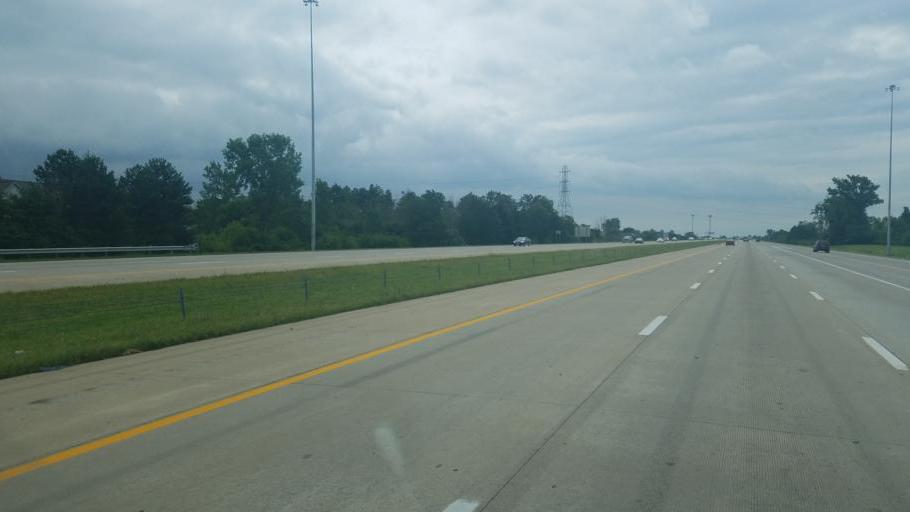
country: US
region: Ohio
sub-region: Franklin County
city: Lincoln Village
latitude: 39.9202
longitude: -83.1165
